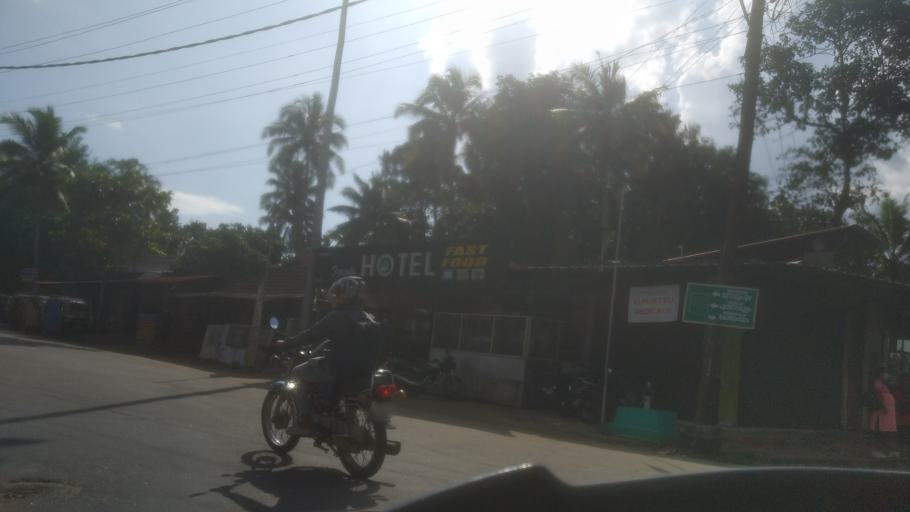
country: IN
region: Kerala
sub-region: Ernakulam
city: Muvattupula
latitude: 9.9987
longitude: 76.6269
